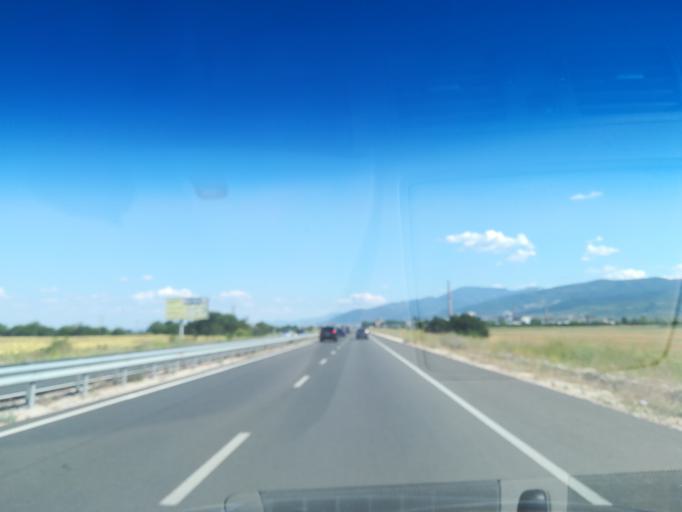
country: BG
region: Plovdiv
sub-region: Obshtina Asenovgrad
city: Asenovgrad
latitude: 42.0760
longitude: 24.8054
